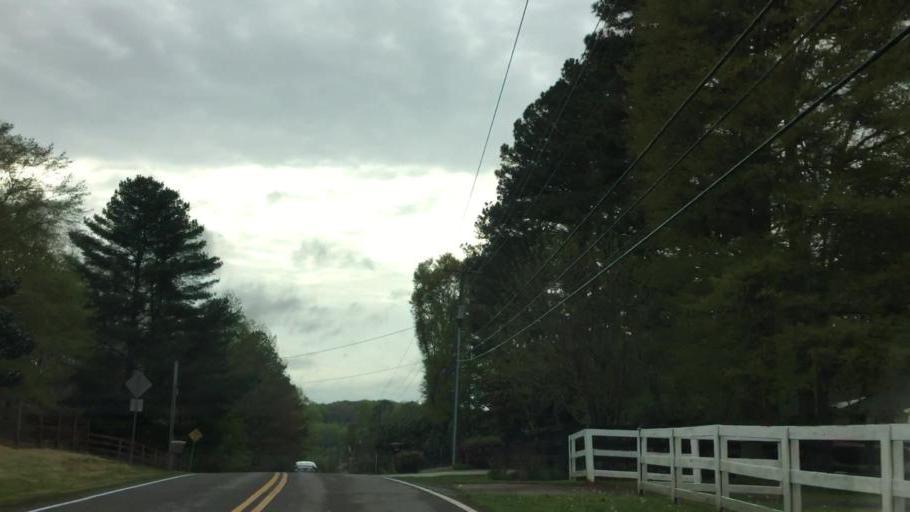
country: US
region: Georgia
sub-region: Fulton County
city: Milton
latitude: 34.1989
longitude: -84.3612
